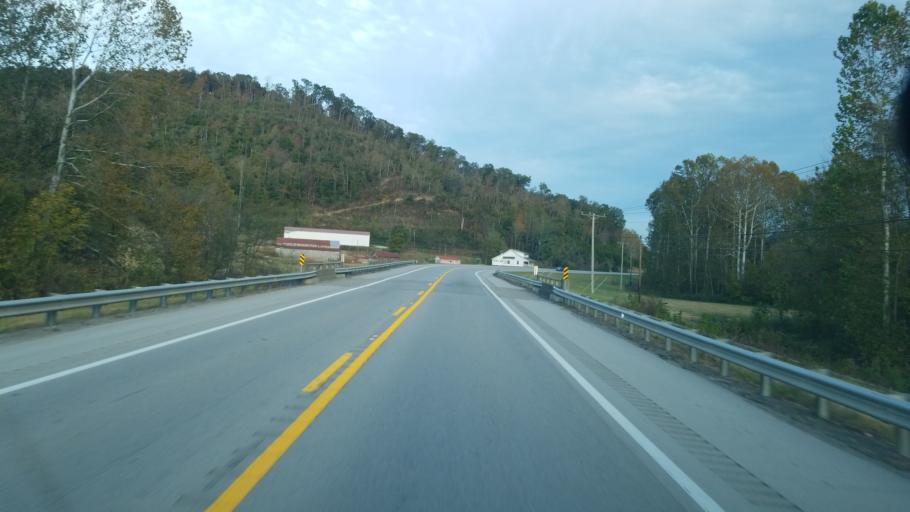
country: US
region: Kentucky
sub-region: Lewis County
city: Vanceburg
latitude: 38.5867
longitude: -83.4107
